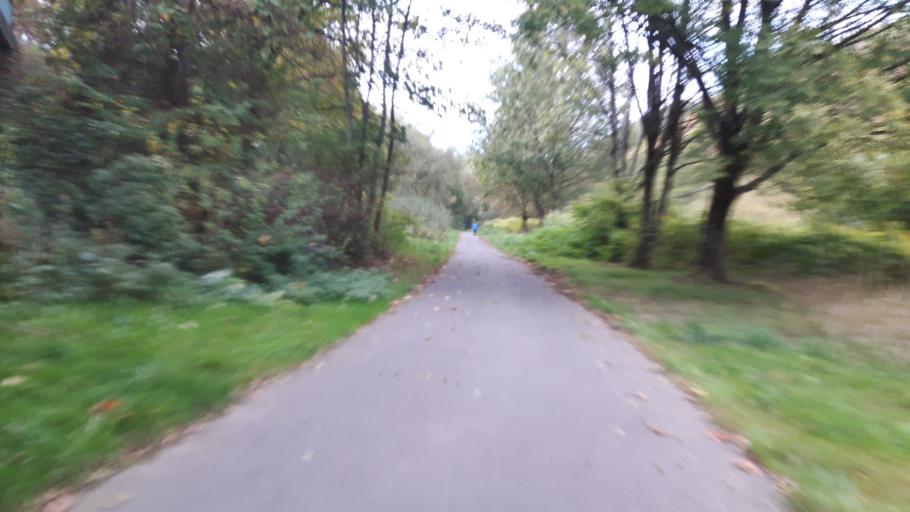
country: DE
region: Rheinland-Pfalz
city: Werkhausen
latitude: 50.7733
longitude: 7.5209
